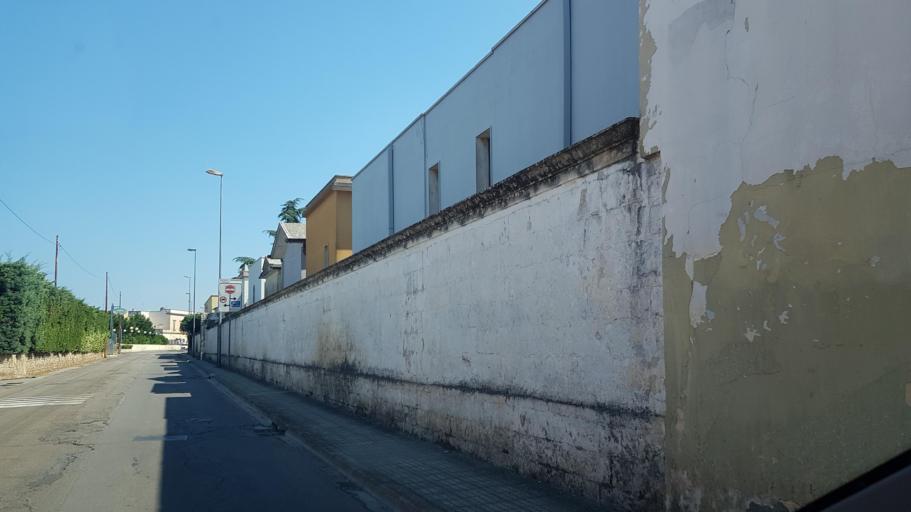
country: IT
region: Apulia
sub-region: Provincia di Lecce
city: Taurisano
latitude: 39.9607
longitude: 18.2109
